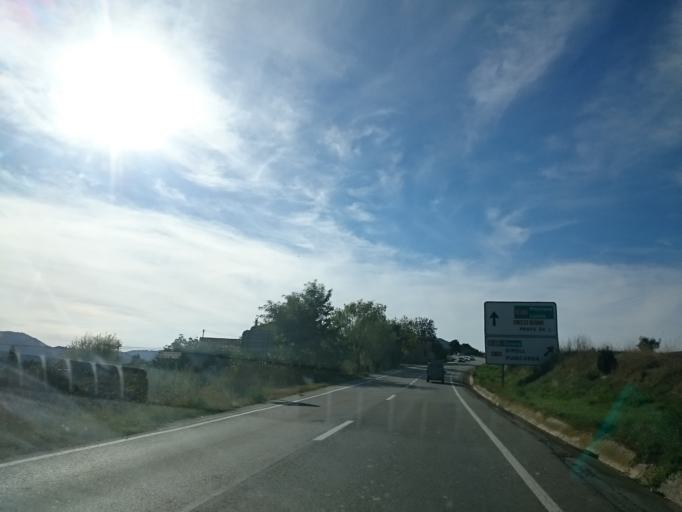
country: ES
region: Catalonia
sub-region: Provincia de Barcelona
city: Vic
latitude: 41.9272
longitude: 2.2354
